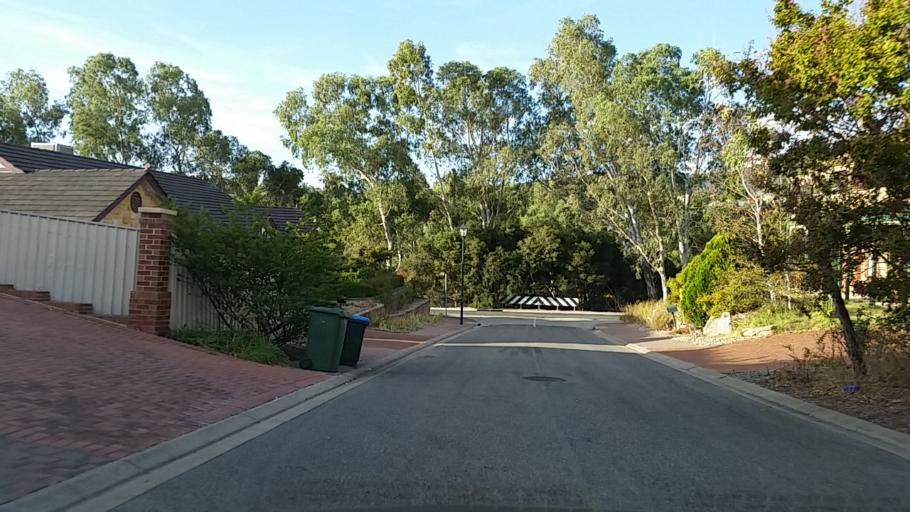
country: AU
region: South Australia
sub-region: Campbelltown
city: Athelstone
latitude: -34.8611
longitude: 138.7128
